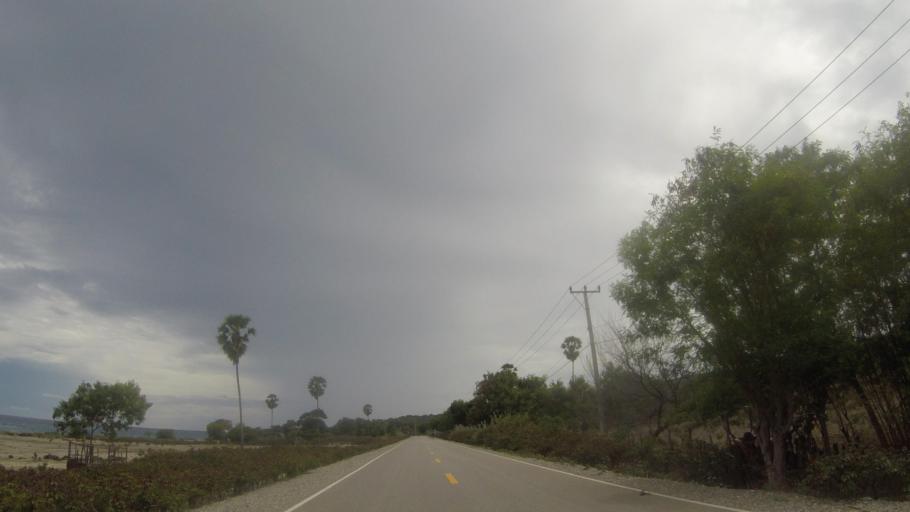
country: TL
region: Baucau
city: Baucau
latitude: -8.4294
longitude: 126.6870
